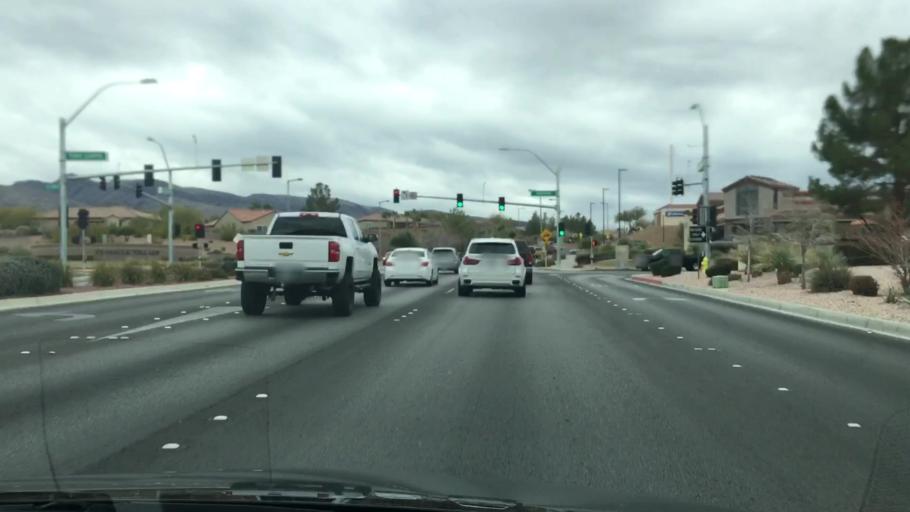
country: US
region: Nevada
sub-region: Clark County
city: Whitney
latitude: 35.9550
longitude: -115.0937
